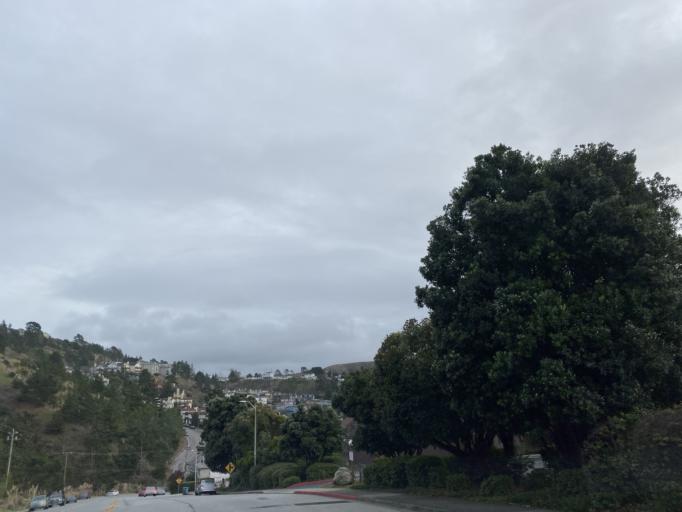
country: US
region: California
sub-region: San Mateo County
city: Colma
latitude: 37.6527
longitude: -122.4821
